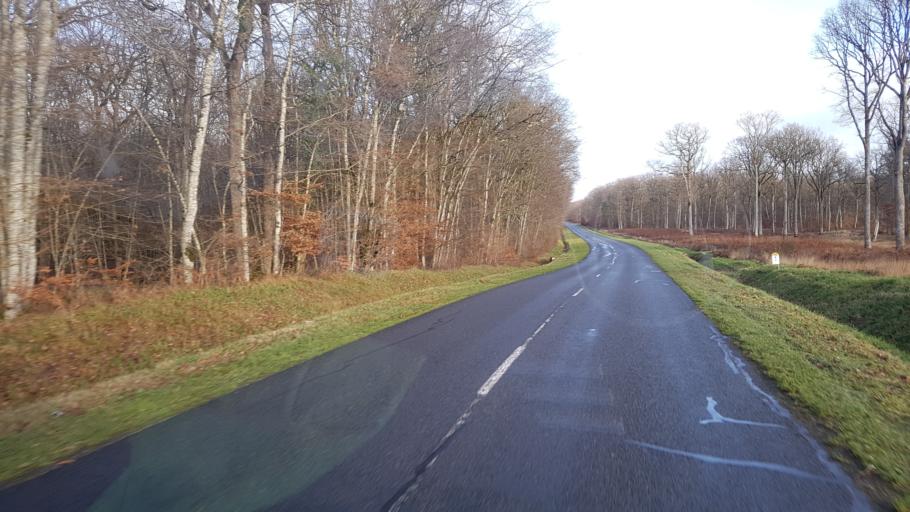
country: FR
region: Centre
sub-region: Departement du Loiret
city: Chilleurs-aux-Bois
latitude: 48.0263
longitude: 2.2099
